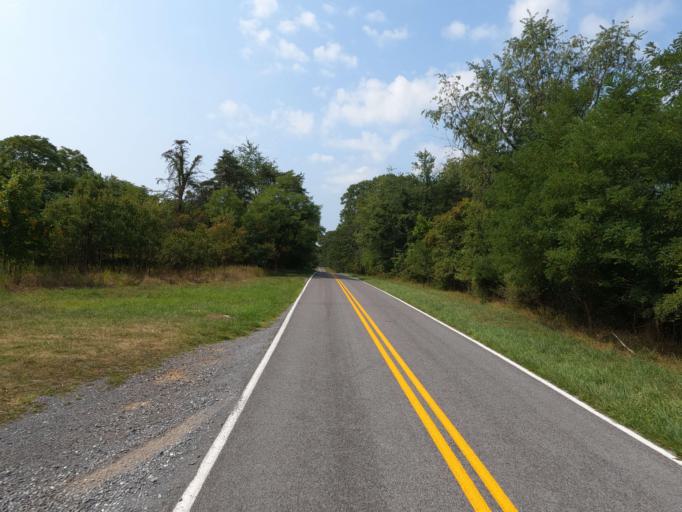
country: US
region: West Virginia
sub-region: Morgan County
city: Berkeley Springs
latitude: 39.6502
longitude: -78.2941
